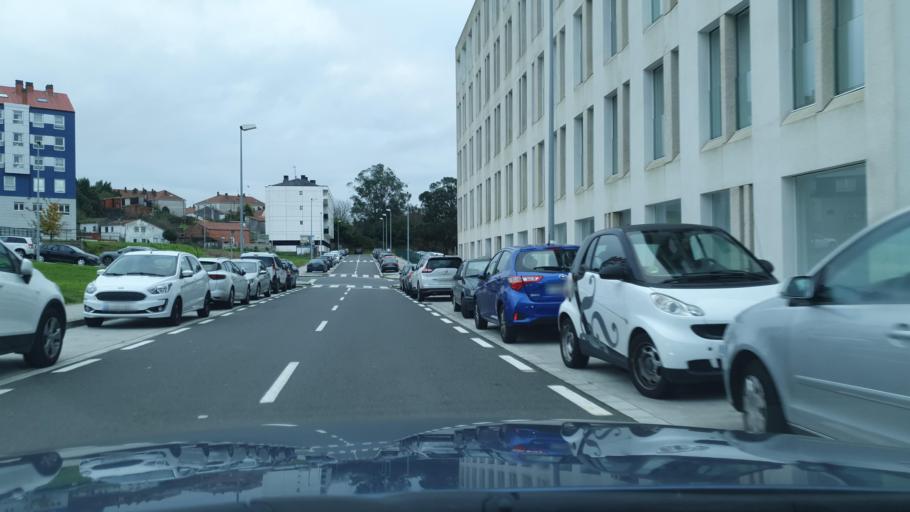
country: ES
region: Galicia
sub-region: Provincia da Coruna
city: Santiago de Compostela
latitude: 42.8673
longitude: -8.5601
